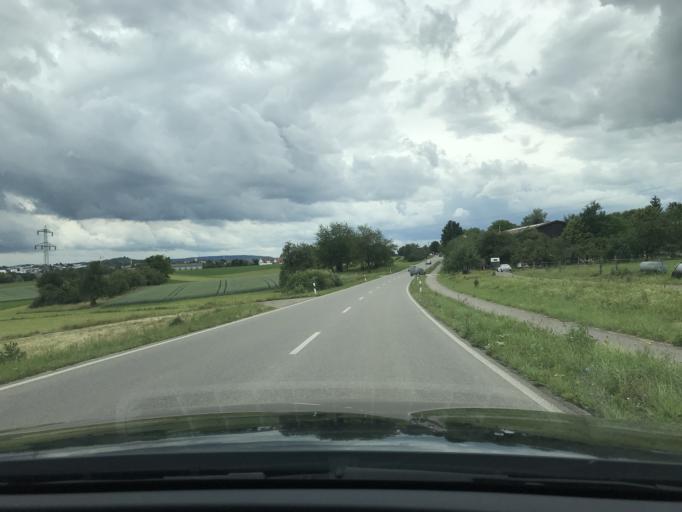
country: DE
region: Baden-Wuerttemberg
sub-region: Regierungsbezirk Stuttgart
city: Schwaikheim
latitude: 48.8860
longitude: 9.3577
